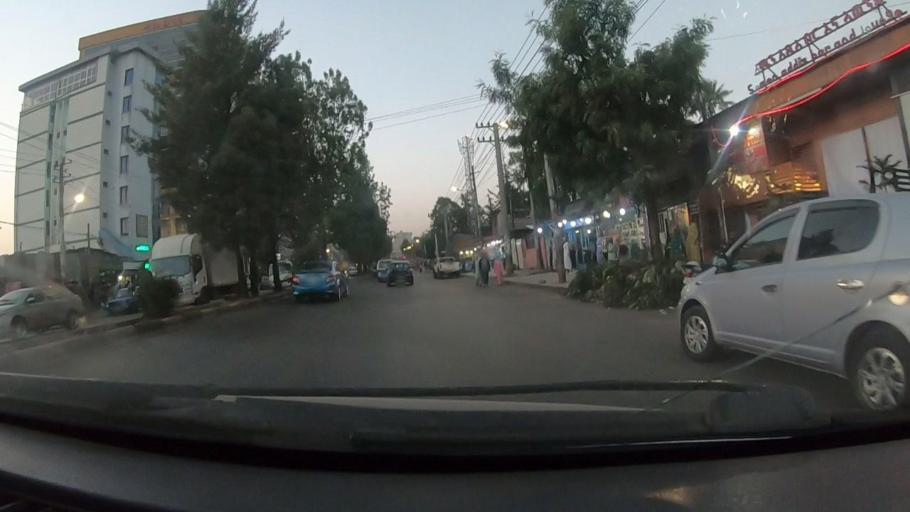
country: ET
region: Adis Abeba
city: Addis Ababa
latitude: 9.0451
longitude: 38.7482
